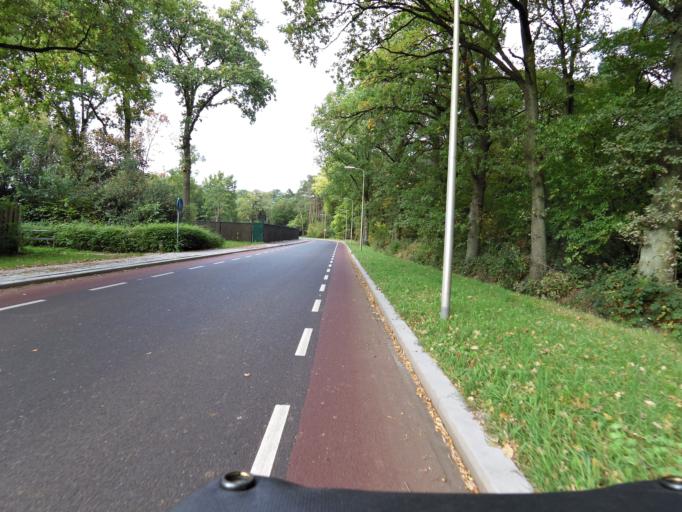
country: BE
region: Flanders
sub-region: Provincie Antwerpen
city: Stabroek
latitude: 51.3653
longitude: 4.3996
